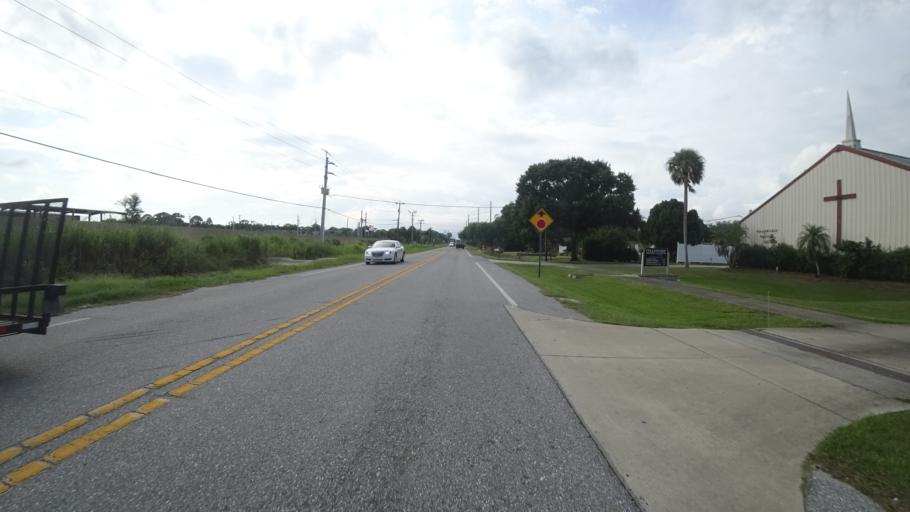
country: US
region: Florida
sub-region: Manatee County
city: Samoset
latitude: 27.4291
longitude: -82.5203
